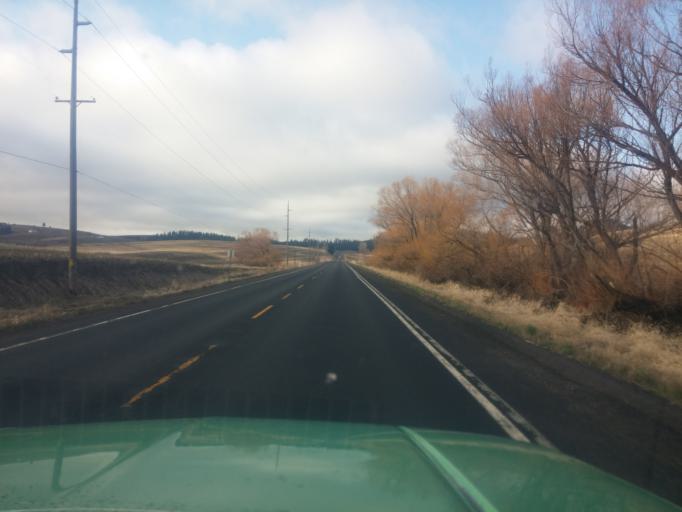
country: US
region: Idaho
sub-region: Latah County
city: Moscow
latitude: 46.8945
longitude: -116.9922
